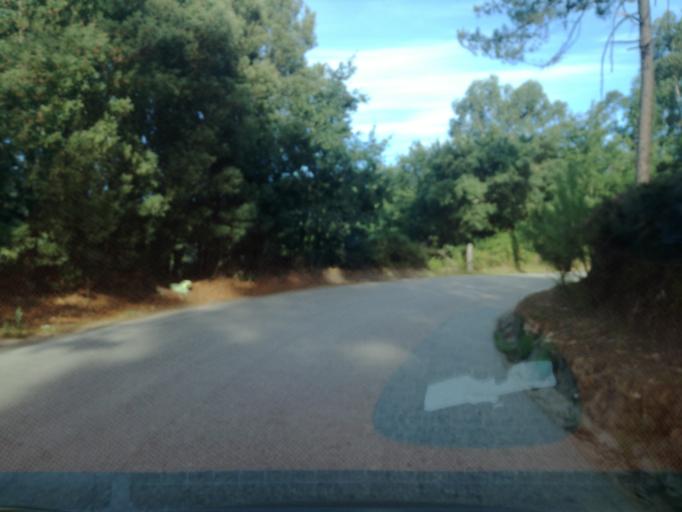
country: PT
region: Porto
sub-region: Valongo
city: Alfena
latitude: 41.2657
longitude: -8.5267
